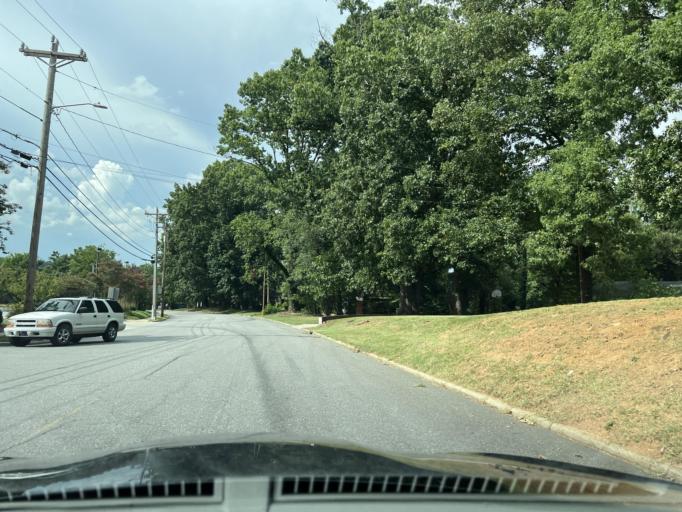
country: US
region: North Carolina
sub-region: Iredell County
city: Statesville
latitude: 35.8007
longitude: -80.8768
